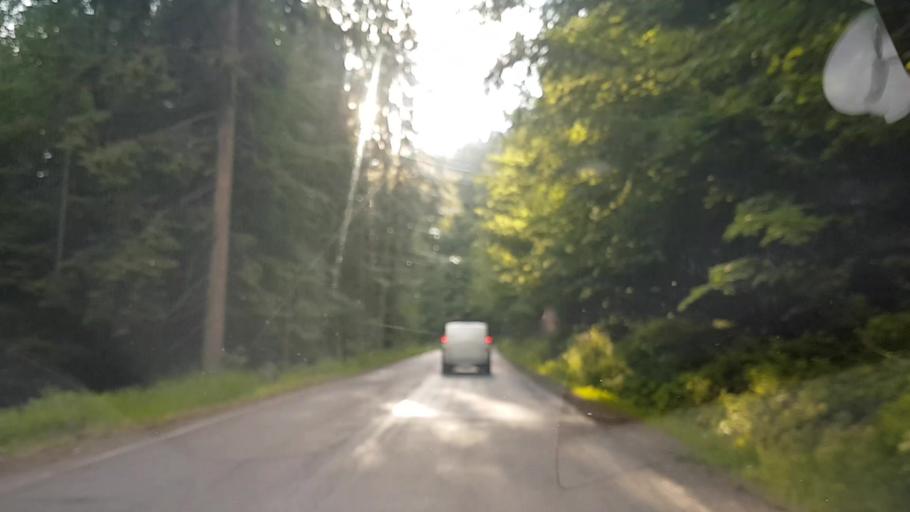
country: RO
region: Harghita
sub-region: Comuna Varsag
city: Varsag
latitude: 46.6655
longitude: 25.3125
